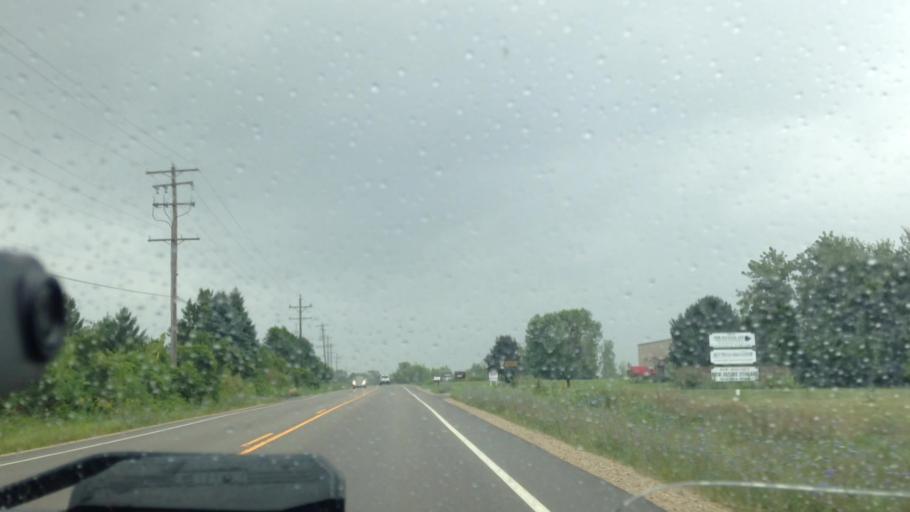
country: US
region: Wisconsin
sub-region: Washington County
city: Richfield
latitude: 43.2865
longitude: -88.2152
